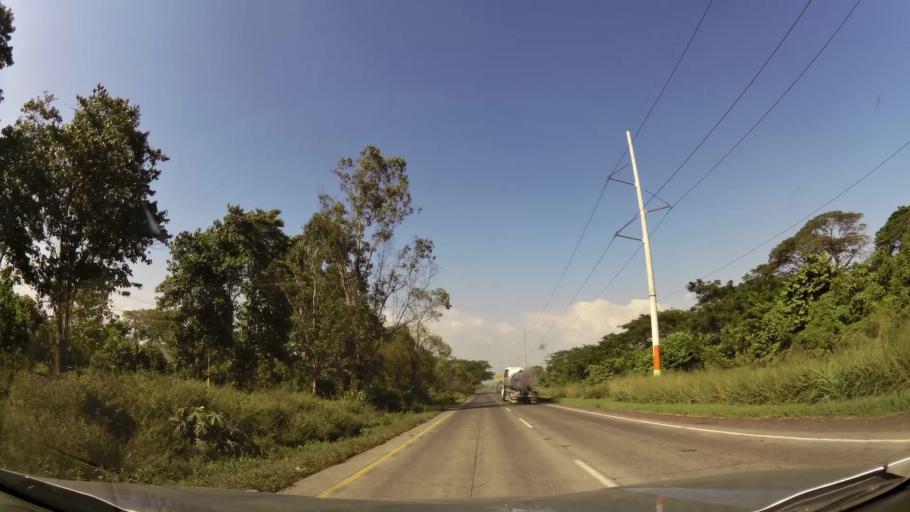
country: GT
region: Escuintla
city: Puerto San Jose
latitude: 13.9516
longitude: -90.7884
